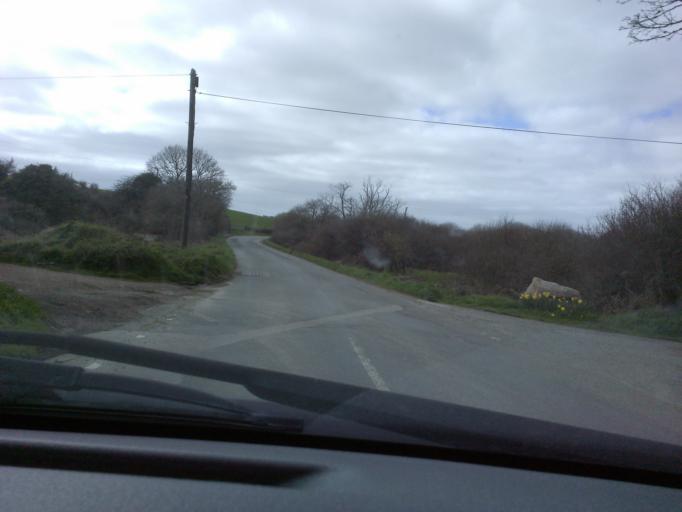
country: GB
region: England
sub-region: Cornwall
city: St. Buryan
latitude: 50.0784
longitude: -5.5716
